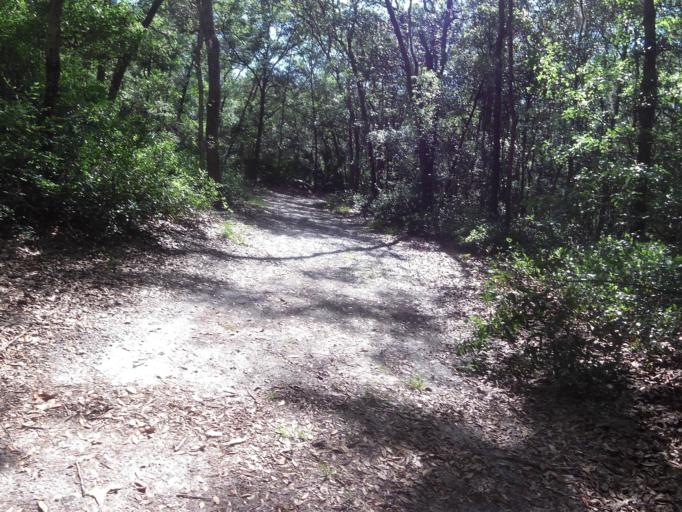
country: US
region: Florida
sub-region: Duval County
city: Atlantic Beach
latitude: 30.4612
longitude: -81.4878
